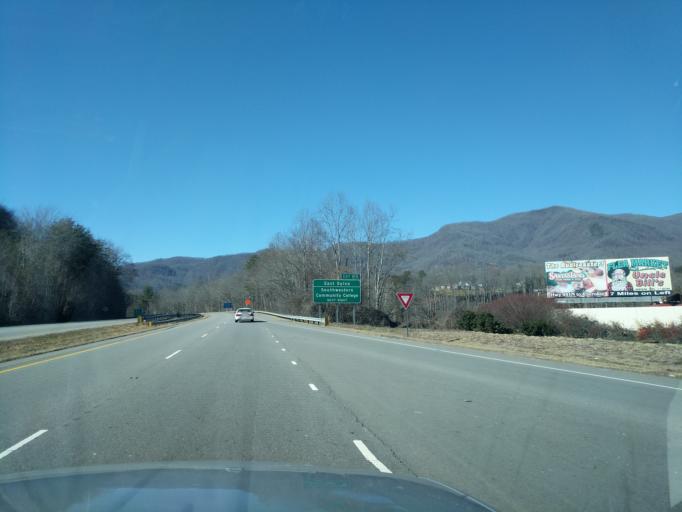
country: US
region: North Carolina
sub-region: Jackson County
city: Sylva
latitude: 35.3920
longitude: -83.1876
